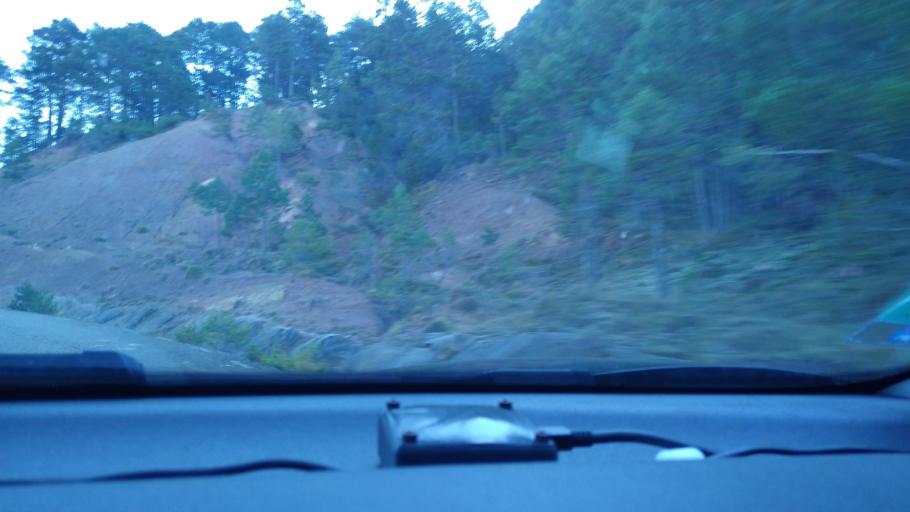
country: ES
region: Catalonia
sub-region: Provincia de Barcelona
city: Saldes
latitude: 42.2044
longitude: 1.7309
